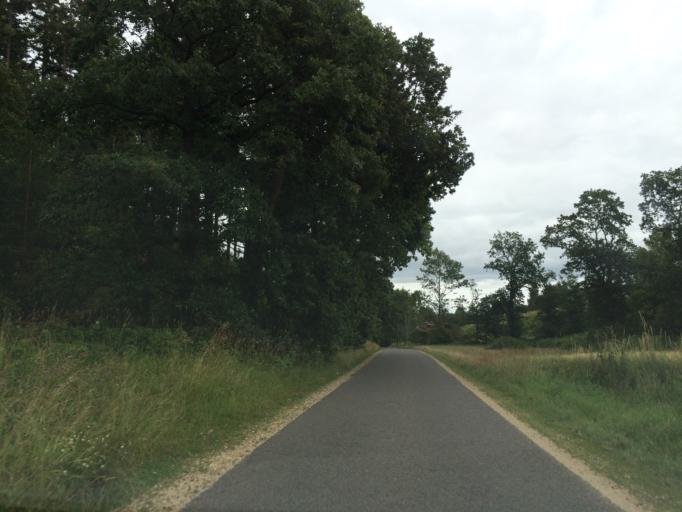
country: DK
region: Central Jutland
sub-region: Silkeborg Kommune
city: Svejbaek
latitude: 56.2053
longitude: 9.6432
